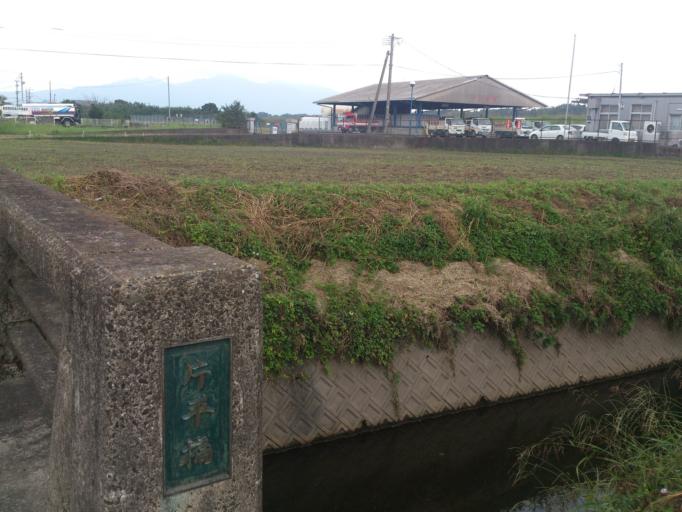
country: JP
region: Kagoshima
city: Kanoya
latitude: 31.3583
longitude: 130.9290
